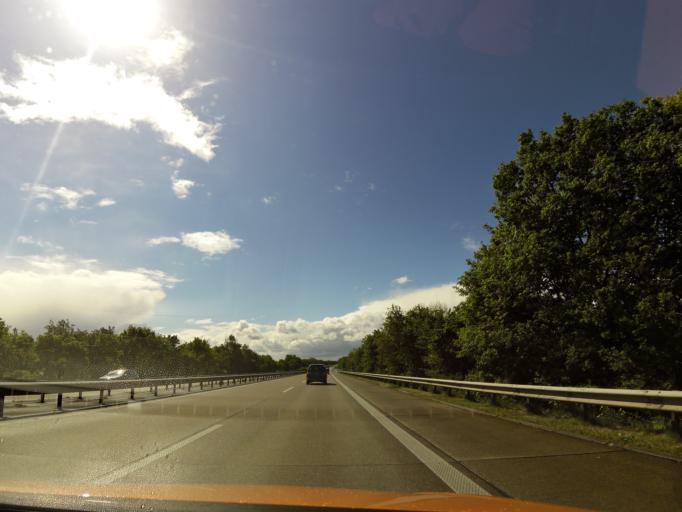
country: DE
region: Lower Saxony
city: Oldenburg
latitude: 53.1448
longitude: 8.2758
